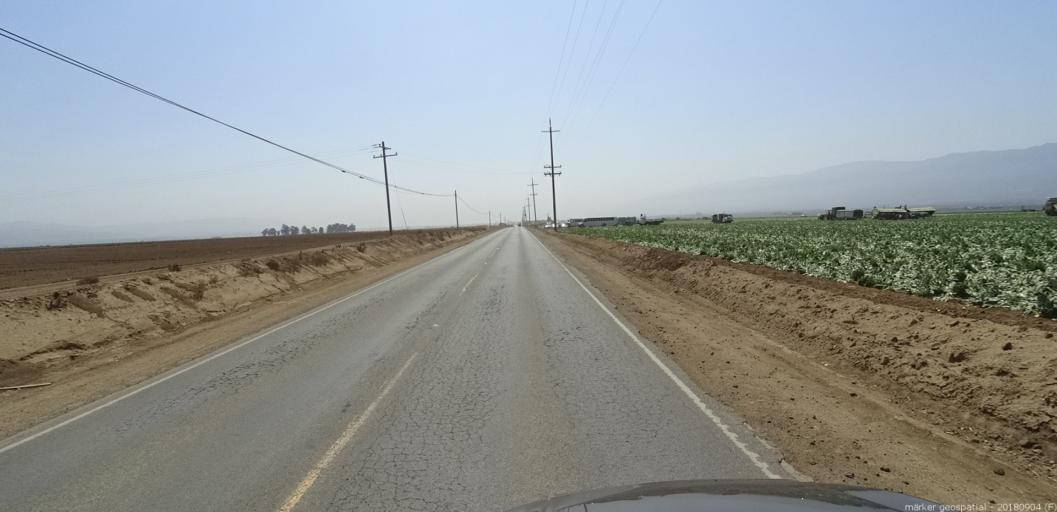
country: US
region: California
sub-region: Monterey County
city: Chualar
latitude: 36.5645
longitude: -121.4844
